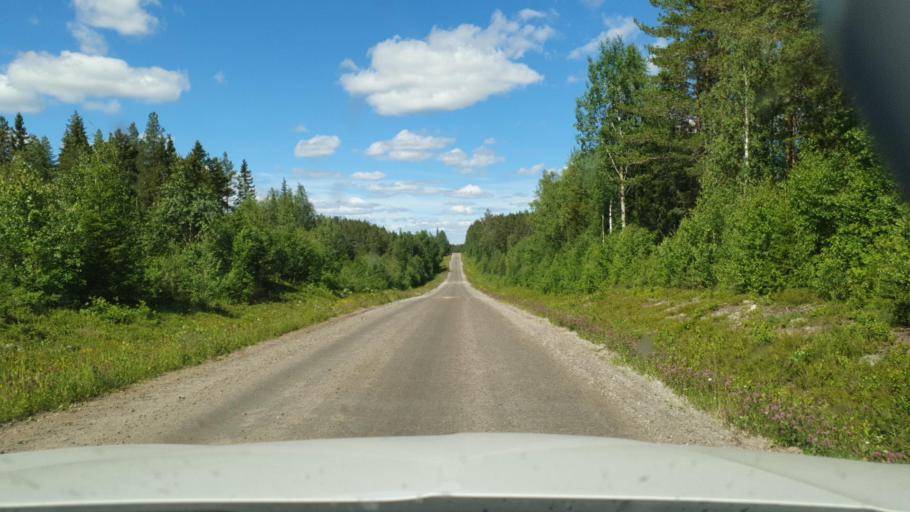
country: SE
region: Vaesterbotten
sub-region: Skelleftea Kommun
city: Byske
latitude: 65.1417
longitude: 21.1779
